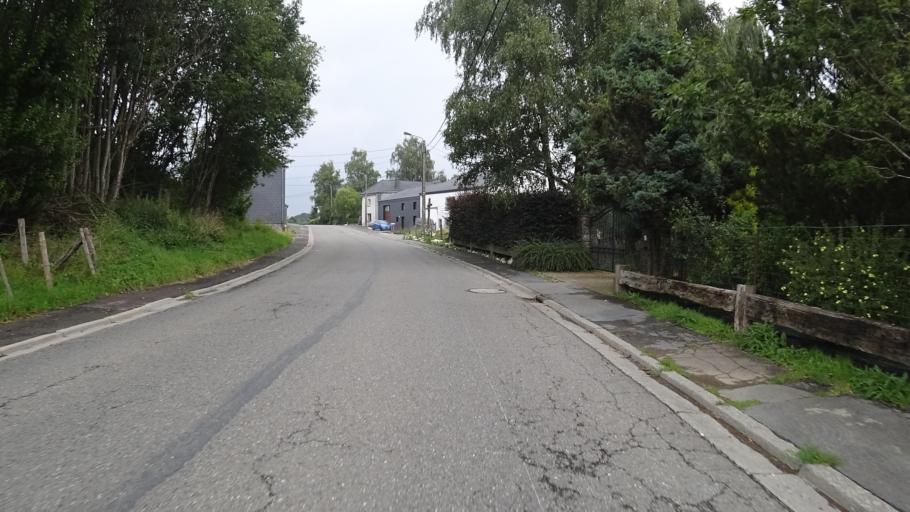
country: BE
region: Wallonia
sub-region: Province du Luxembourg
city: Chiny
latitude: 49.8099
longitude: 5.3285
